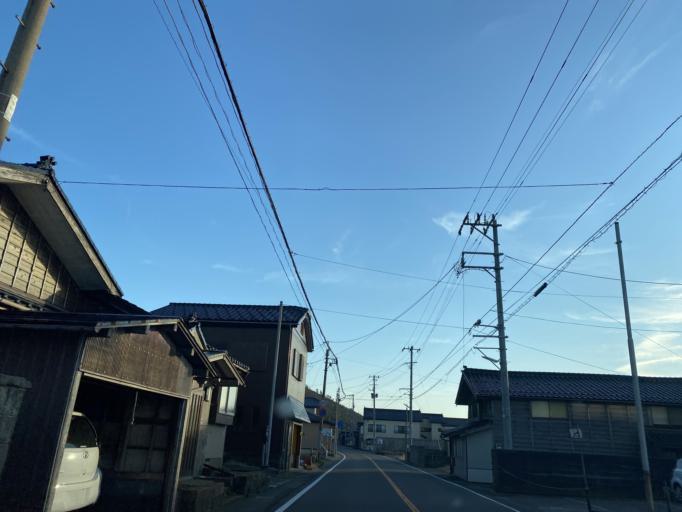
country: JP
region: Niigata
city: Kashiwazaki
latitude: 37.4598
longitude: 138.6112
